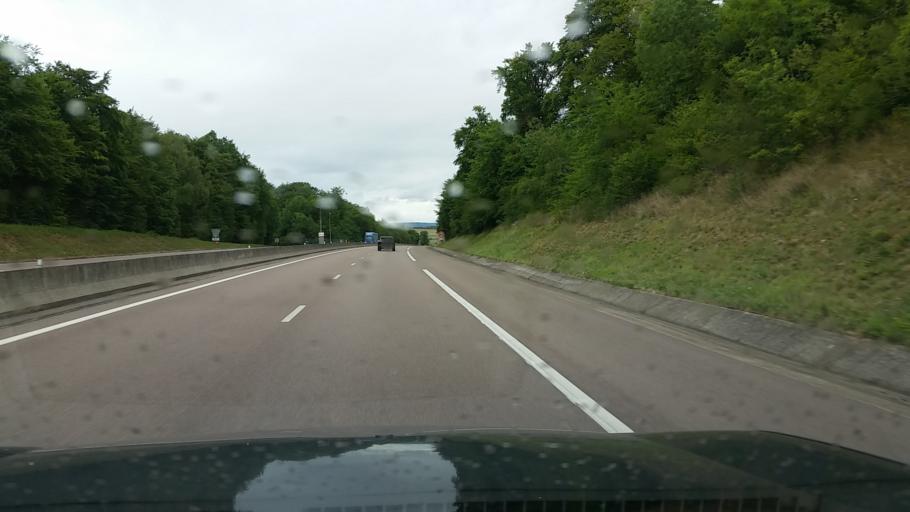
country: FR
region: Lorraine
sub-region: Departement de Meurthe-et-Moselle
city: Colombey-les-Belles
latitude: 48.4240
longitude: 5.8606
